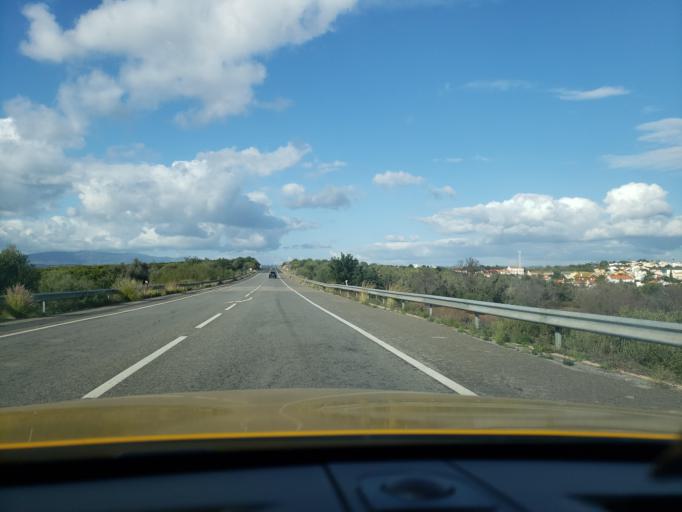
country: PT
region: Faro
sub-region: Silves
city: Silves
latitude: 37.1706
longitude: -8.4427
